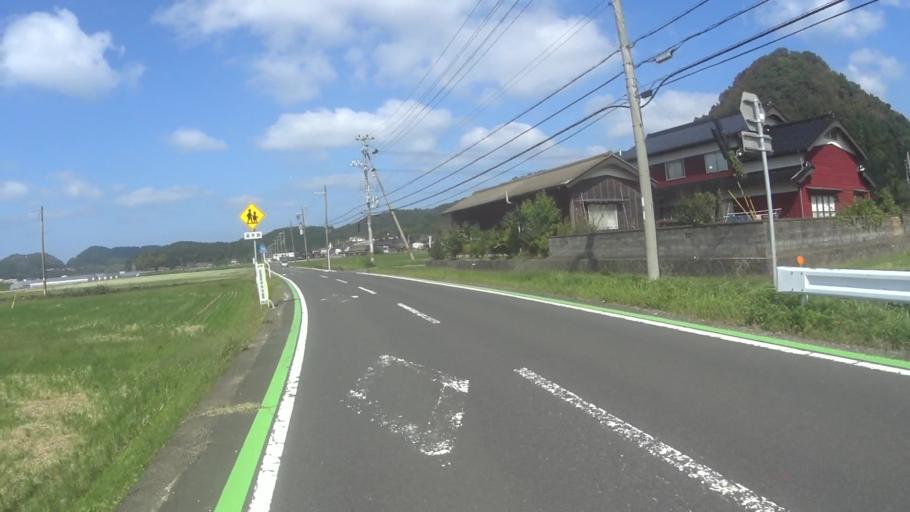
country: JP
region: Kyoto
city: Miyazu
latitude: 35.7182
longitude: 135.1079
